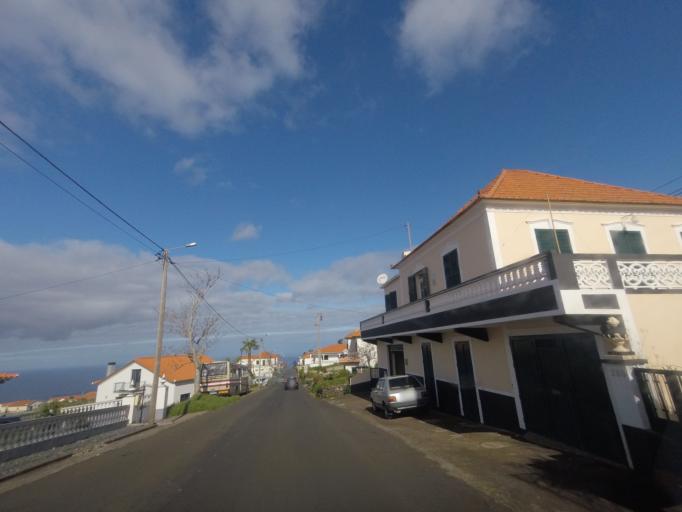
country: PT
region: Madeira
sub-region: Calheta
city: Faja da Ovelha
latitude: 32.8095
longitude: -17.2443
